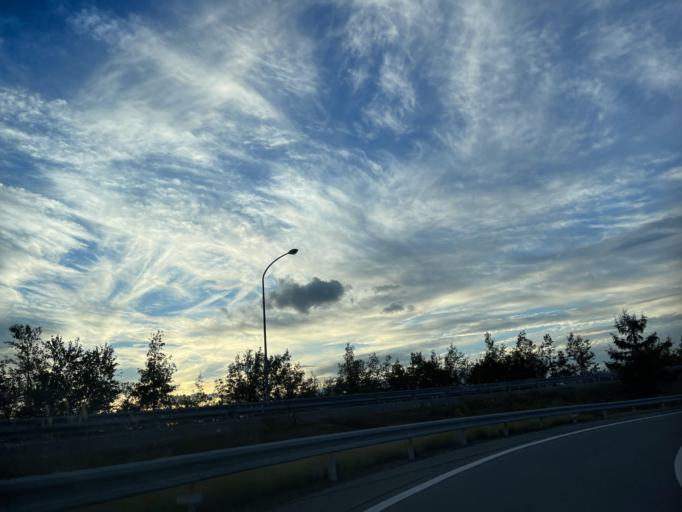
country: JP
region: Nagano
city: Komoro
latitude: 36.3447
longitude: 138.4080
